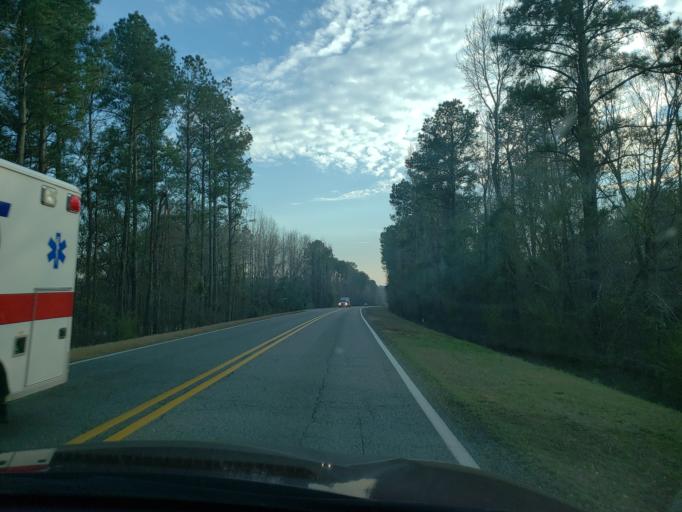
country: US
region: Alabama
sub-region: Hale County
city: Greensboro
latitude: 32.7314
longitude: -87.5872
